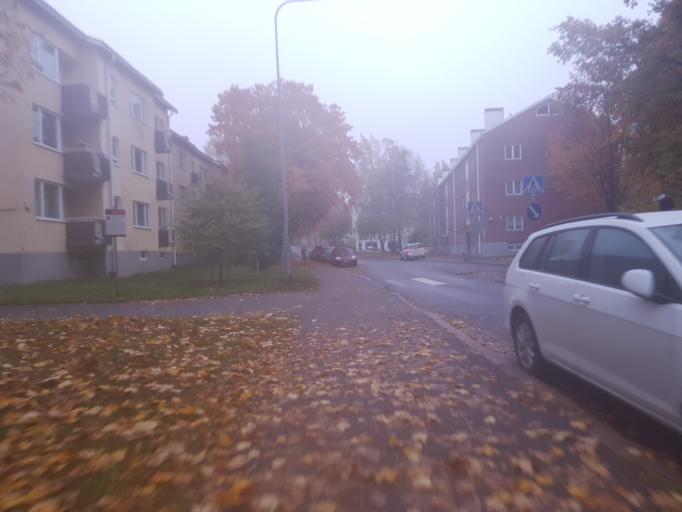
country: FI
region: Uusimaa
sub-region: Helsinki
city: Helsinki
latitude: 60.2271
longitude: 24.9277
